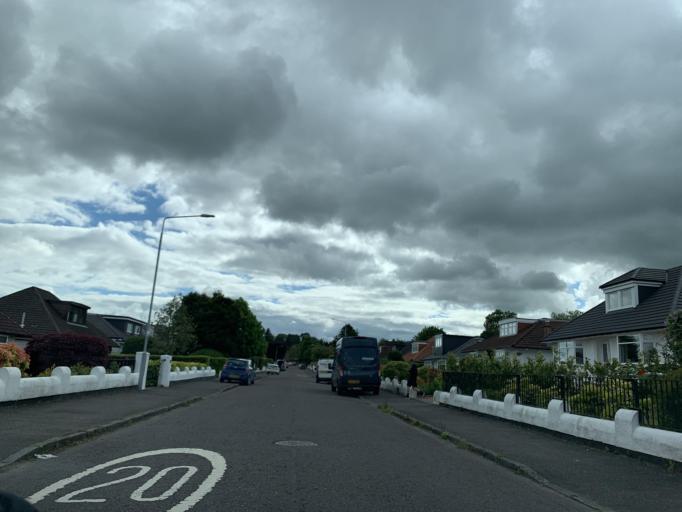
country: GB
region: Scotland
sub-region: East Renfrewshire
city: Newton Mearns
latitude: 55.7751
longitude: -4.3255
